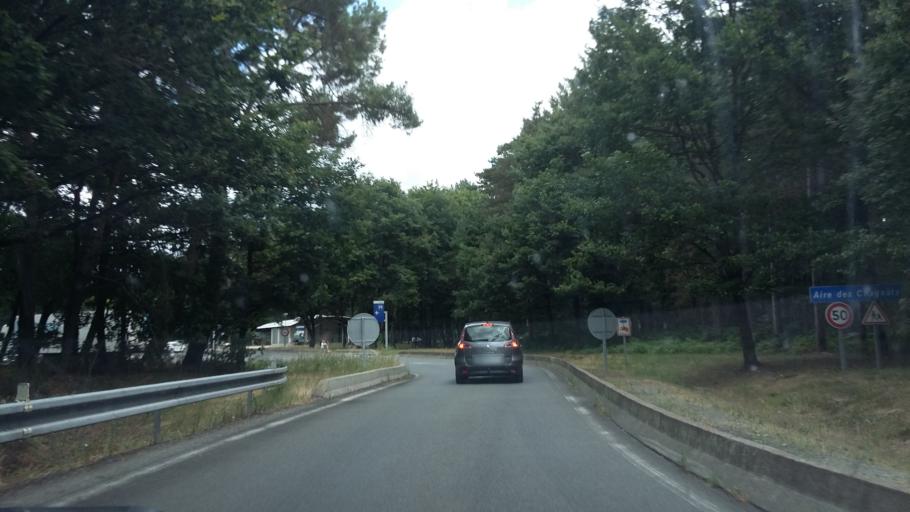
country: FR
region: Poitou-Charentes
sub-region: Departement de la Vienne
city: Chatellerault
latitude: 46.7934
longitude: 0.5106
